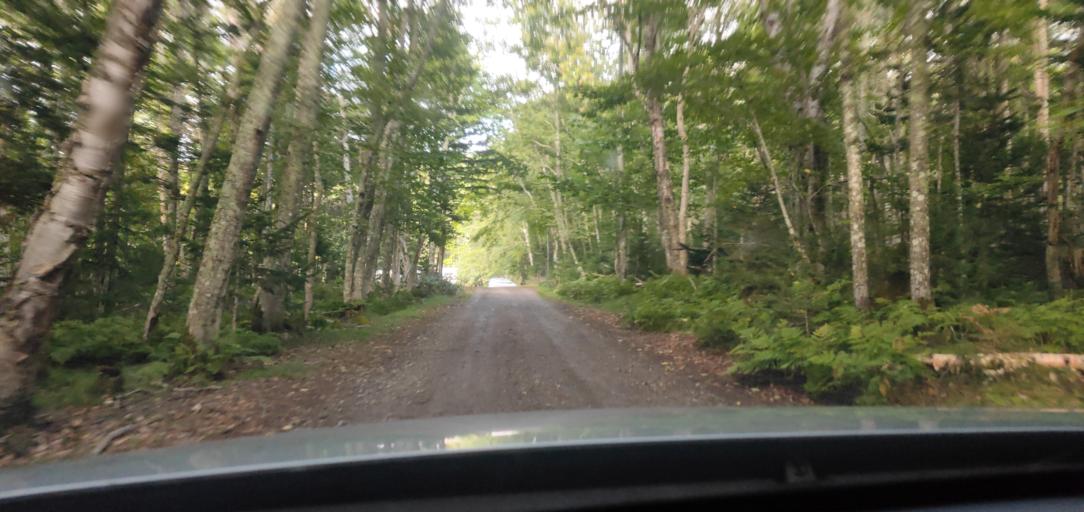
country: JP
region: Hokkaido
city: Kitami
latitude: 43.3801
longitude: 143.9715
